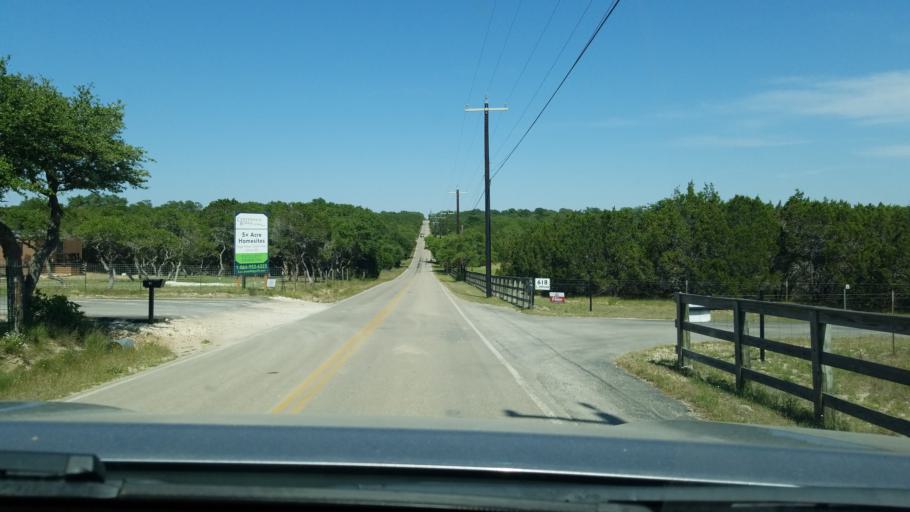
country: US
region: Texas
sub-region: Comal County
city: Bulverde
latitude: 29.7591
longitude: -98.4968
